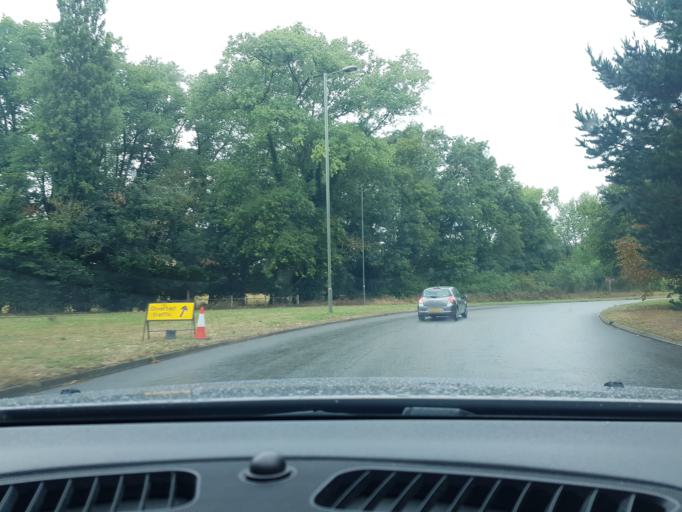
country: GB
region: England
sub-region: Surrey
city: Hale
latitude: 51.2250
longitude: -0.7832
